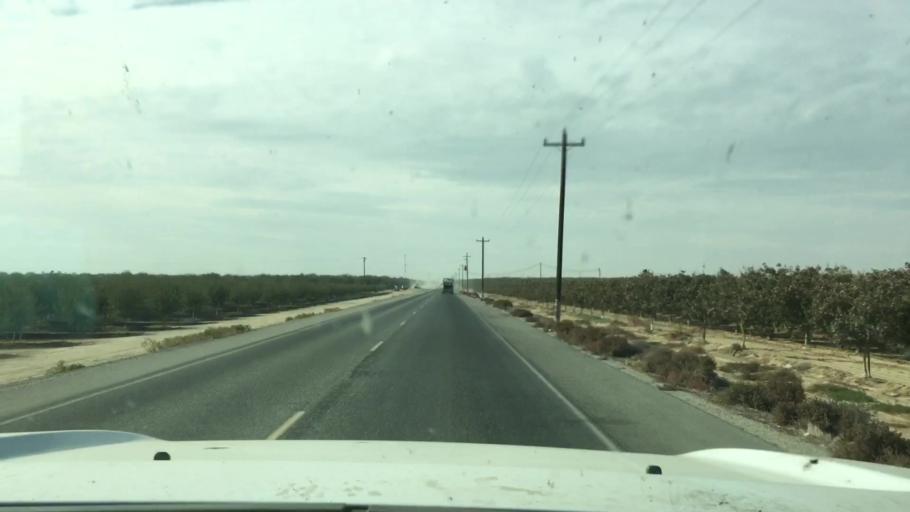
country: US
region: California
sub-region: Kern County
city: Buttonwillow
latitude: 35.5005
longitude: -119.4806
